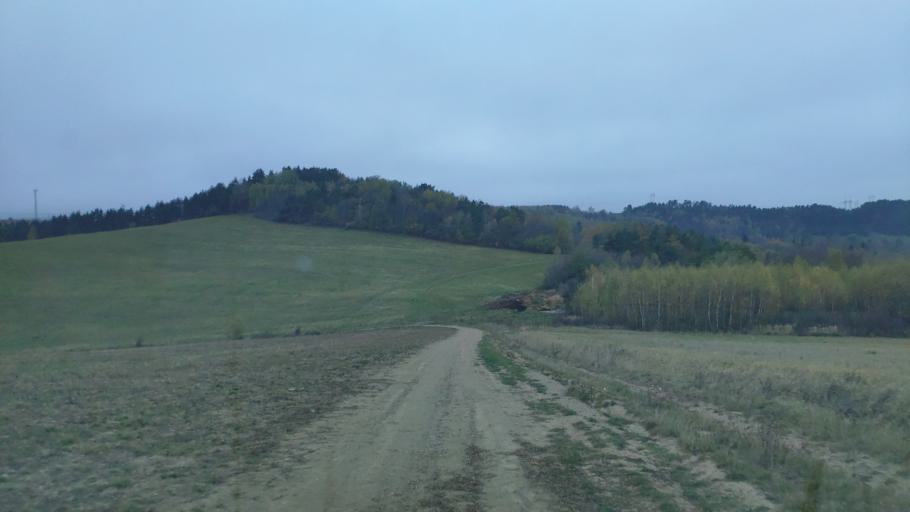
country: SK
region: Presovsky
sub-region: Okres Presov
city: Presov
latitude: 48.9326
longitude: 21.0878
